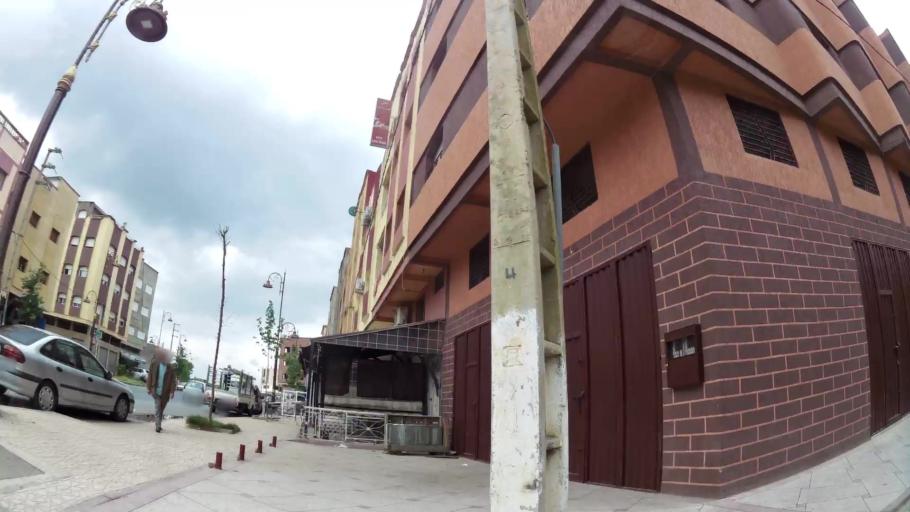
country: MA
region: Rabat-Sale-Zemmour-Zaer
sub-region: Khemisset
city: Tiflet
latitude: 33.8856
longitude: -6.3199
